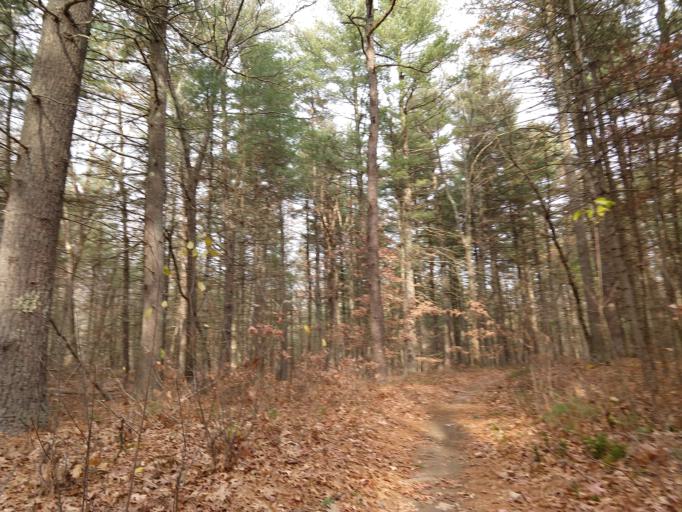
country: US
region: Massachusetts
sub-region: Middlesex County
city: Billerica
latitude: 42.5832
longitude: -71.3049
